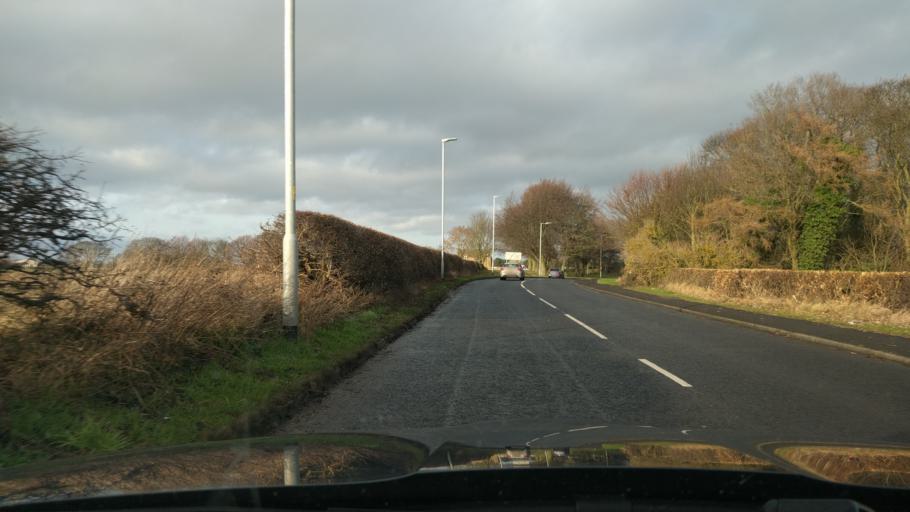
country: GB
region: England
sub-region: Northumberland
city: Ashington
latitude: 55.1786
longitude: -1.6068
